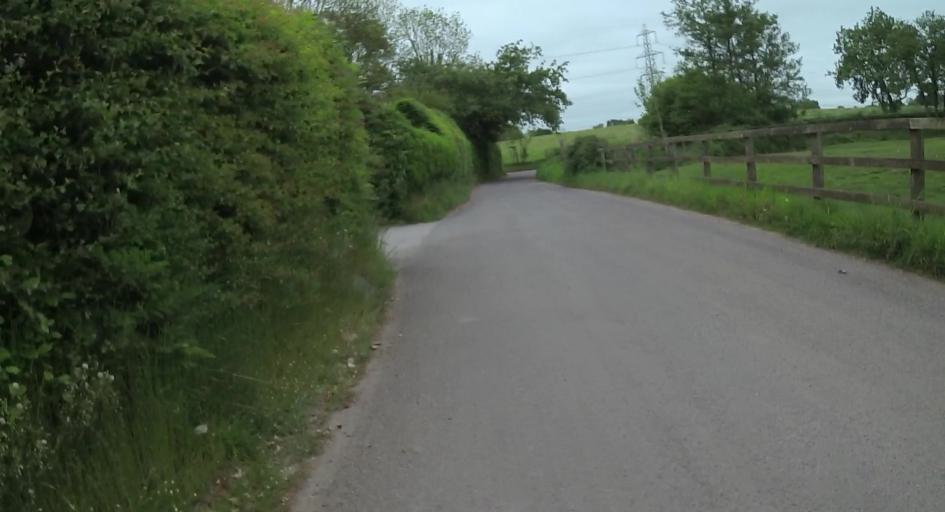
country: GB
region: England
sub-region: West Berkshire
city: Stratfield Mortimer
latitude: 51.3498
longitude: -1.0663
